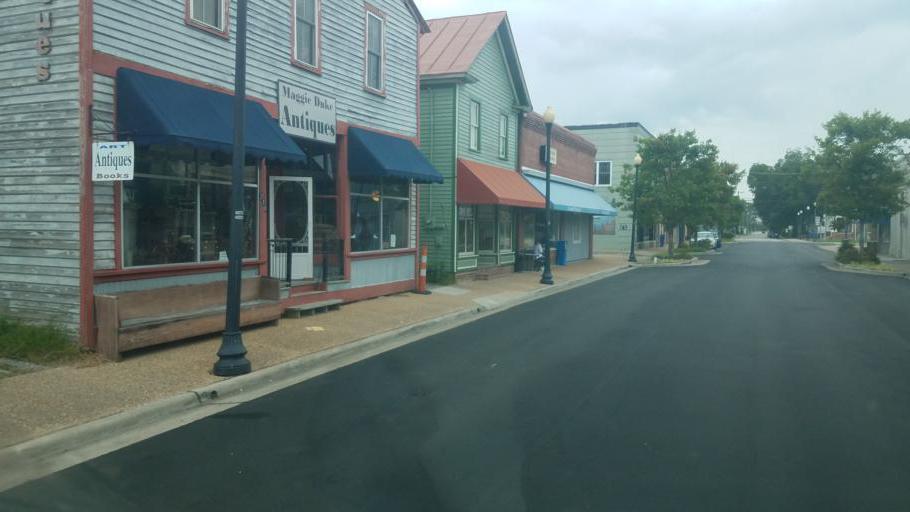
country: US
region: North Carolina
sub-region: Tyrrell County
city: Columbia
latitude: 35.9176
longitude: -76.2535
